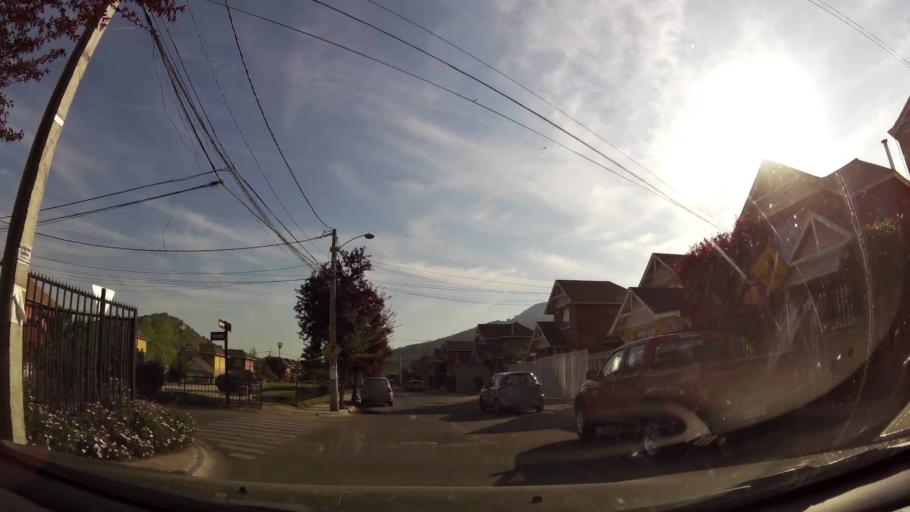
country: CL
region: Santiago Metropolitan
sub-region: Provincia de Cordillera
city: Puente Alto
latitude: -33.5596
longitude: -70.5448
